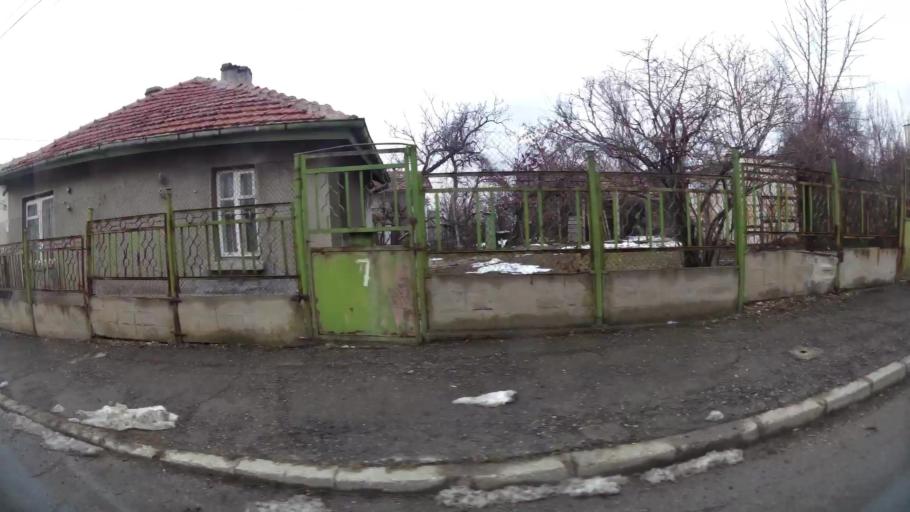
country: BG
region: Sofiya
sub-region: Obshtina Bozhurishte
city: Bozhurishte
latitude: 42.6953
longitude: 23.2212
